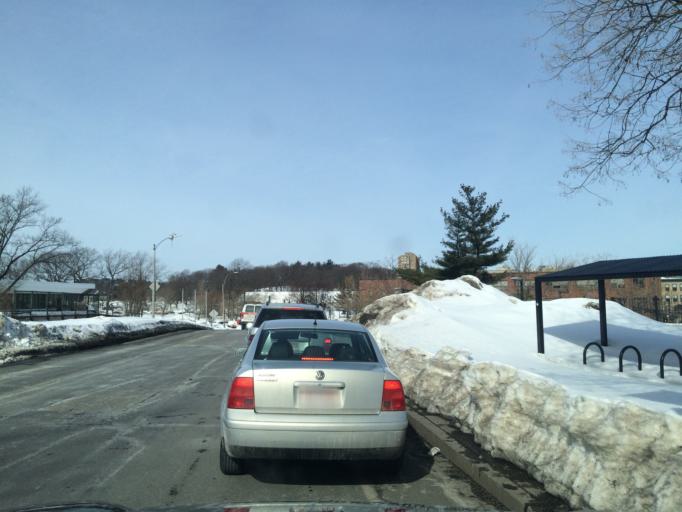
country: US
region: Massachusetts
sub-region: Norfolk County
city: Brookline
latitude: 42.3347
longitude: -71.1489
